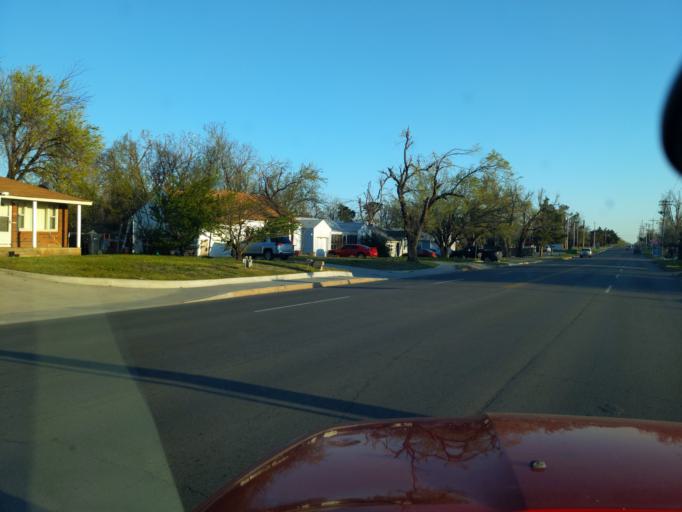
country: US
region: Oklahoma
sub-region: Oklahoma County
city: Oklahoma City
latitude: 35.4182
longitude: -97.5214
